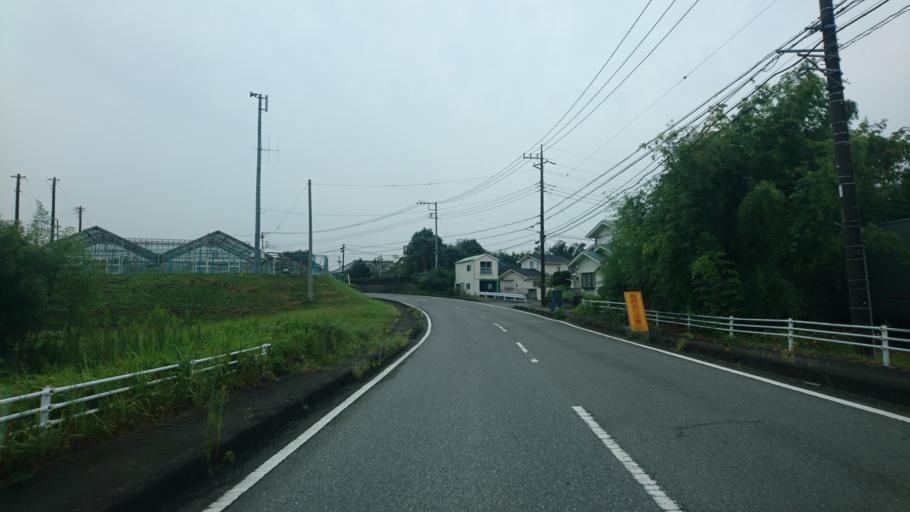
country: JP
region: Chiba
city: Kimitsu
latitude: 35.3097
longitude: 139.9602
